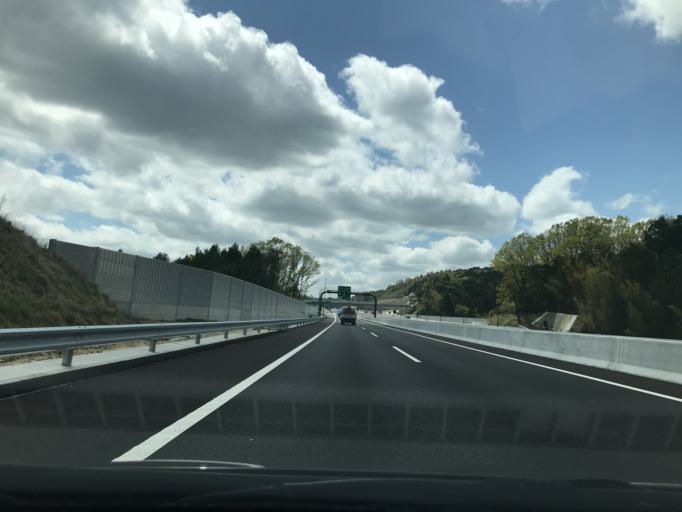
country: JP
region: Osaka
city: Ibaraki
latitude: 34.8880
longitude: 135.5393
